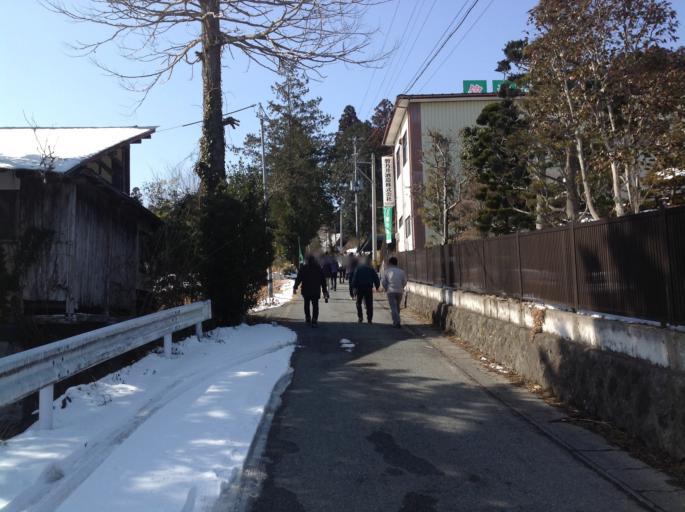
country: JP
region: Iwate
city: Ichinoseki
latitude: 38.8186
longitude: 141.1920
